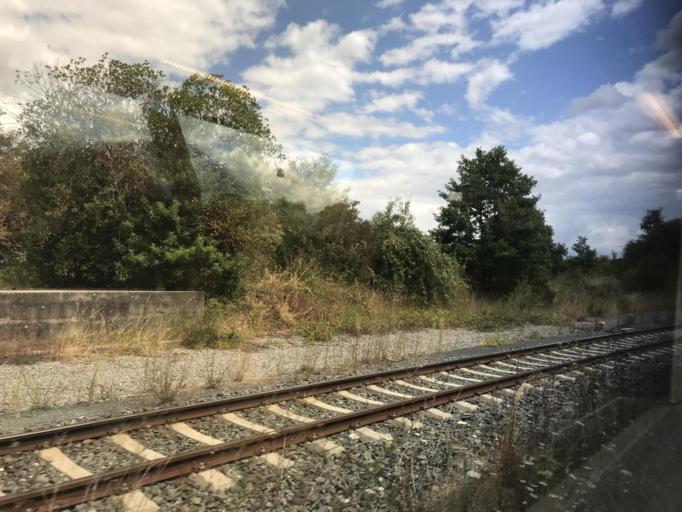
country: DE
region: Bavaria
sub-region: Regierungsbezirk Unterfranken
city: Elfershausen
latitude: 50.1403
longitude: 9.9723
